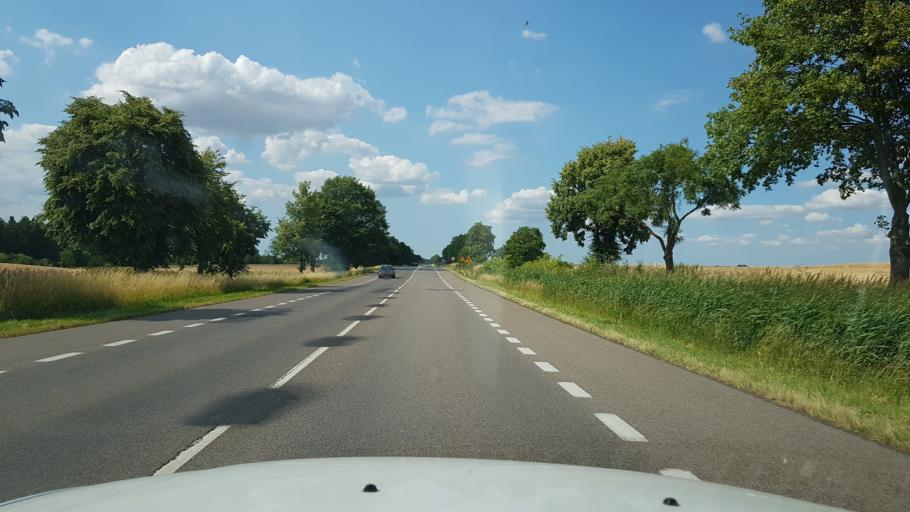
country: PL
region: West Pomeranian Voivodeship
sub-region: Powiat pyrzycki
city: Pyrzyce
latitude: 53.1068
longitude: 14.8974
